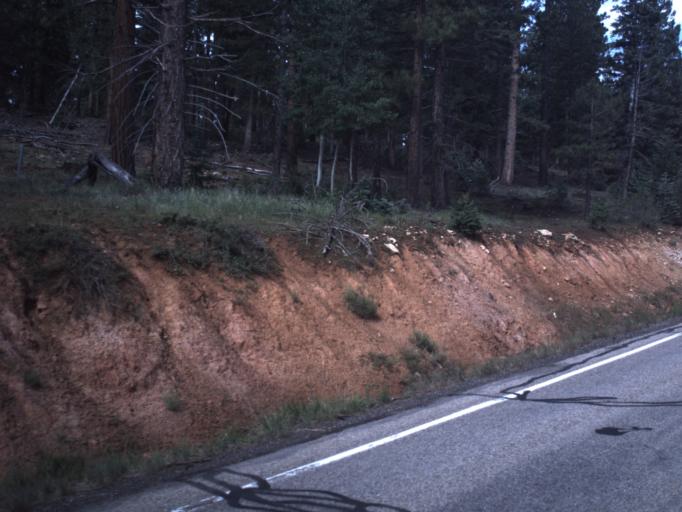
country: US
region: Utah
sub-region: Garfield County
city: Panguitch
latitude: 37.5137
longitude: -112.6361
